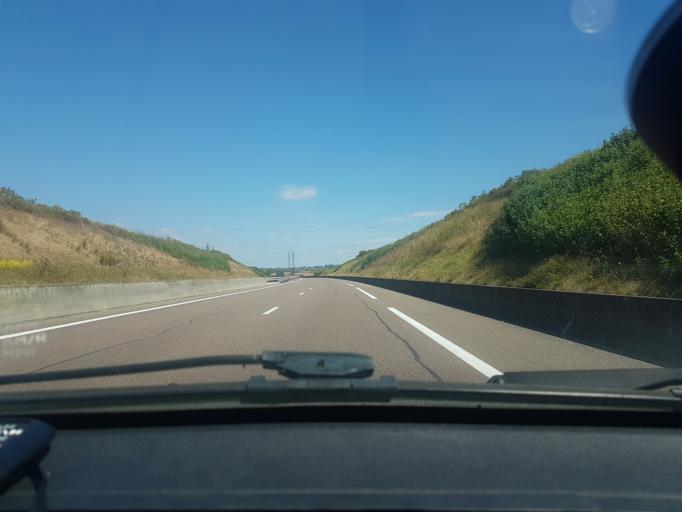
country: FR
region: Bourgogne
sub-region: Departement de la Cote-d'Or
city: Quetigny
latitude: 47.3253
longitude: 5.1012
